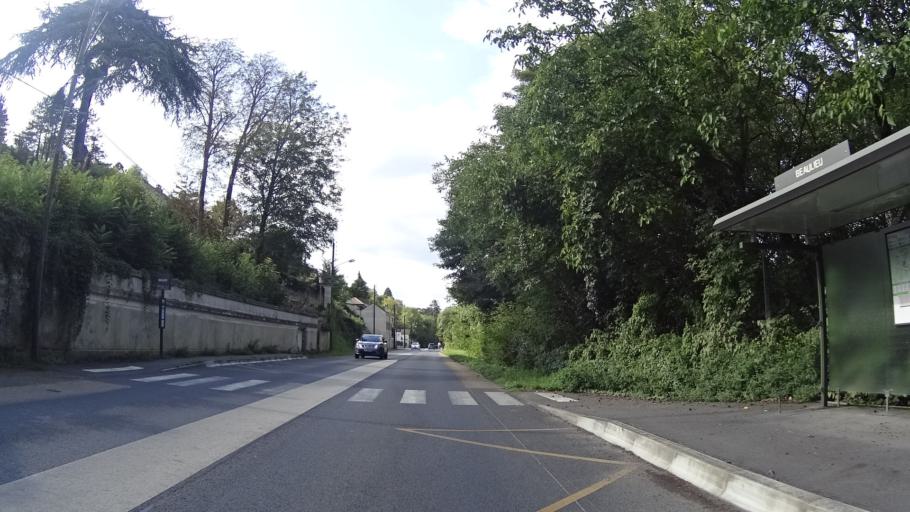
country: FR
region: Pays de la Loire
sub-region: Departement de Maine-et-Loire
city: Villebernier
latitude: 47.2465
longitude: -0.0411
